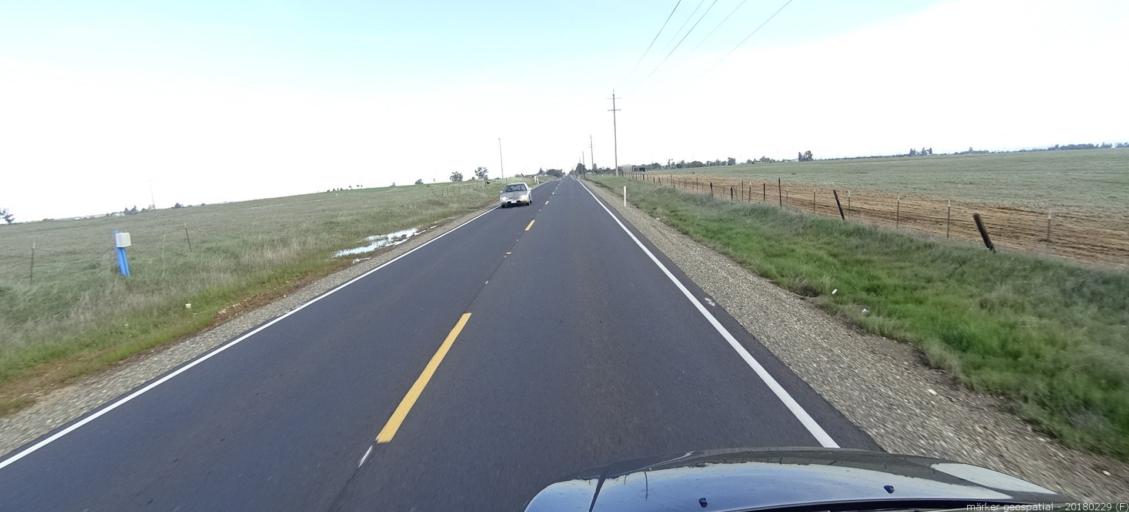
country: US
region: California
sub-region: Sacramento County
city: Vineyard
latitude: 38.5003
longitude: -121.2979
